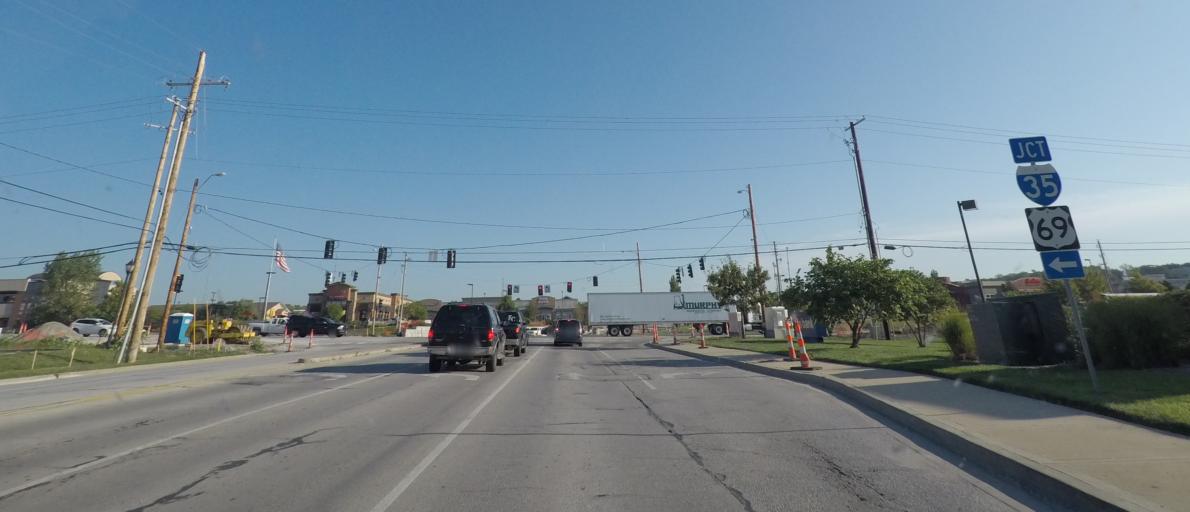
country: US
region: Missouri
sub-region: Clay County
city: Liberty
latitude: 39.2440
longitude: -94.4515
